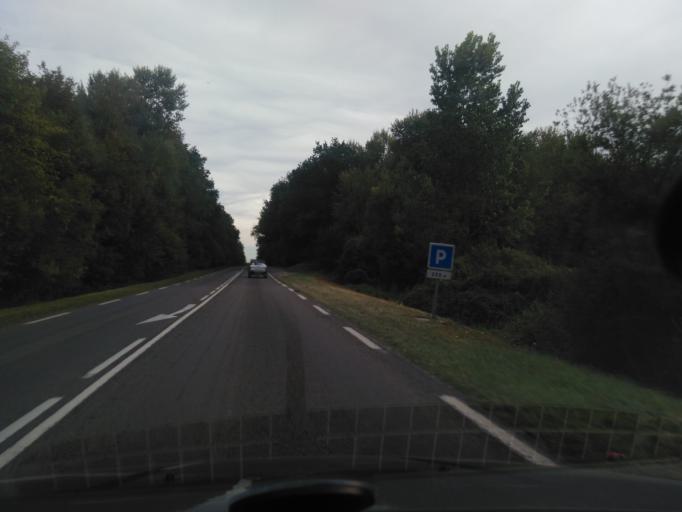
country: FR
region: Picardie
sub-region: Departement de l'Aisne
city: Laon
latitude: 49.5592
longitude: 3.5929
